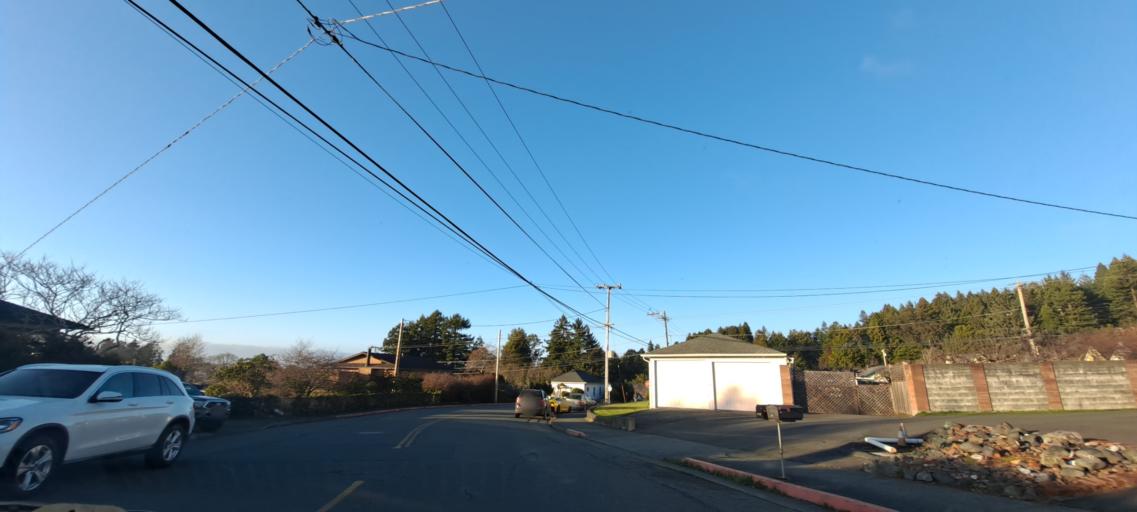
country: US
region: California
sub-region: Humboldt County
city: Arcata
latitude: 40.8682
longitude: -124.0778
